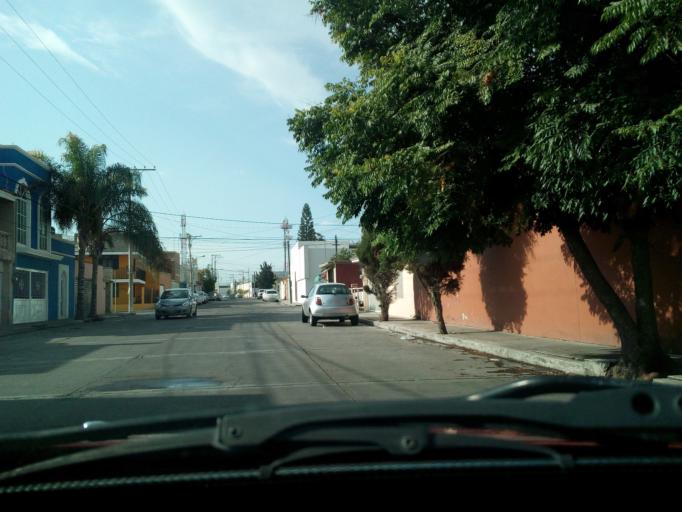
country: MX
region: Aguascalientes
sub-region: Aguascalientes
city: Aguascalientes
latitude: 21.9061
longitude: -102.2948
